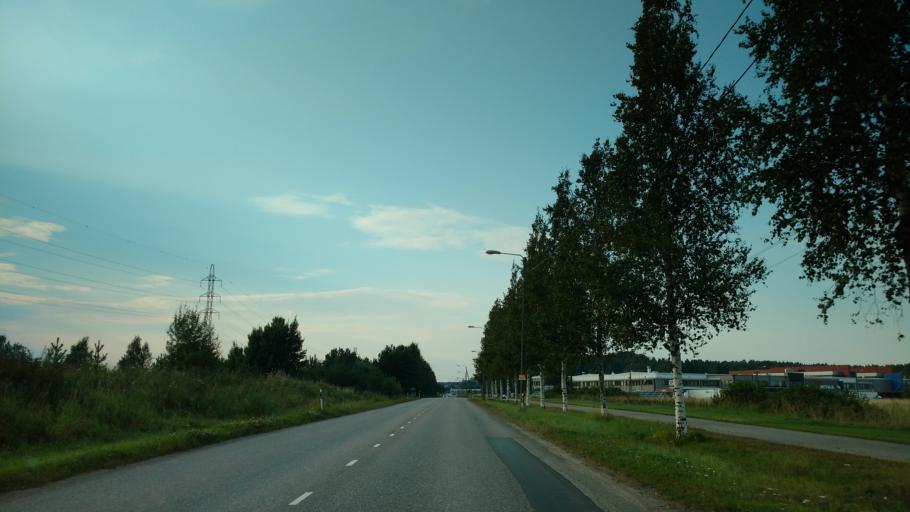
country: FI
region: Varsinais-Suomi
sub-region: Salo
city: Halikko
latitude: 60.3828
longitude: 23.1011
